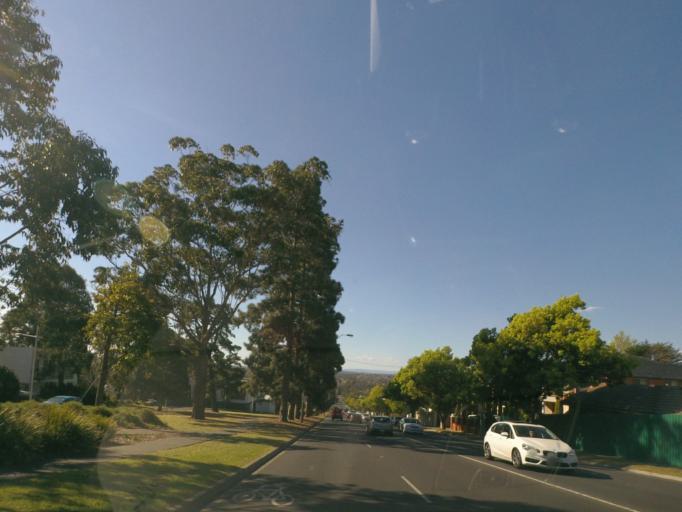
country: AU
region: Victoria
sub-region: Boroondara
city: Kew
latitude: -37.7988
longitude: 145.0302
